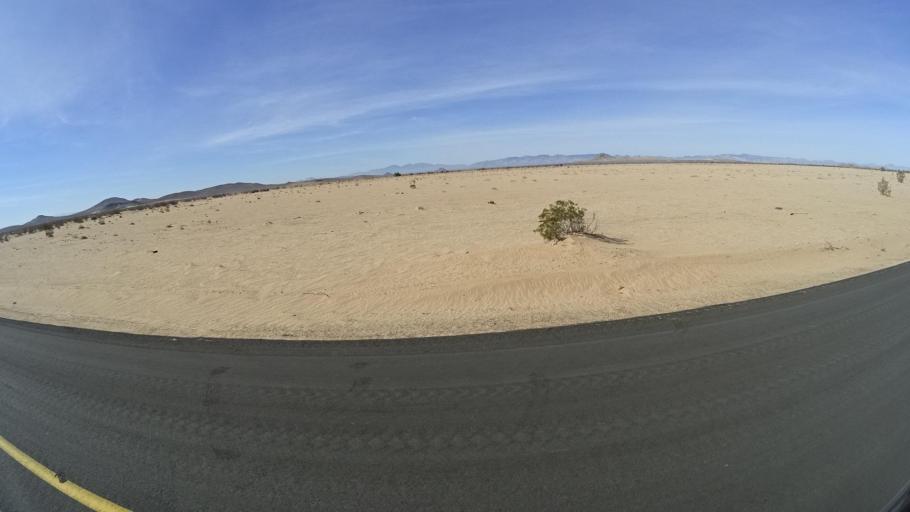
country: US
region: California
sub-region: Kern County
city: North Edwards
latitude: 35.0886
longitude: -117.7926
